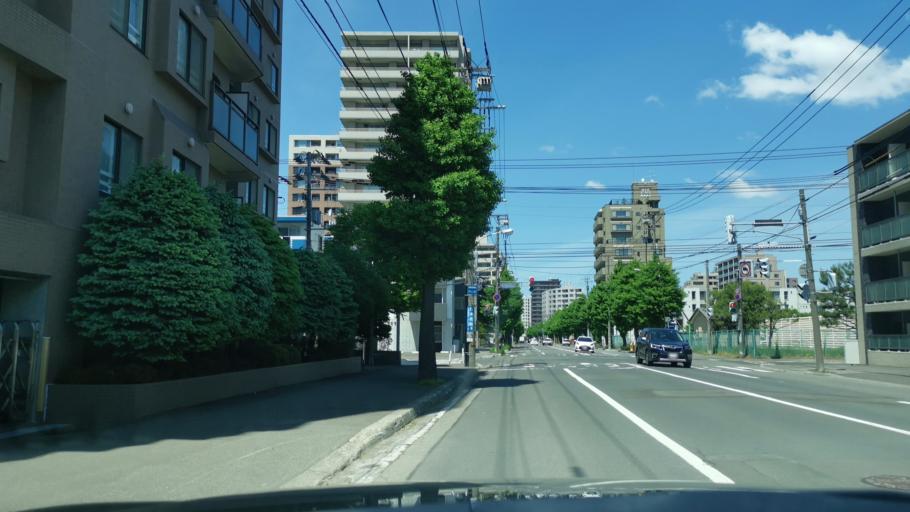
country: JP
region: Hokkaido
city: Sapporo
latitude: 43.0504
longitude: 141.3283
